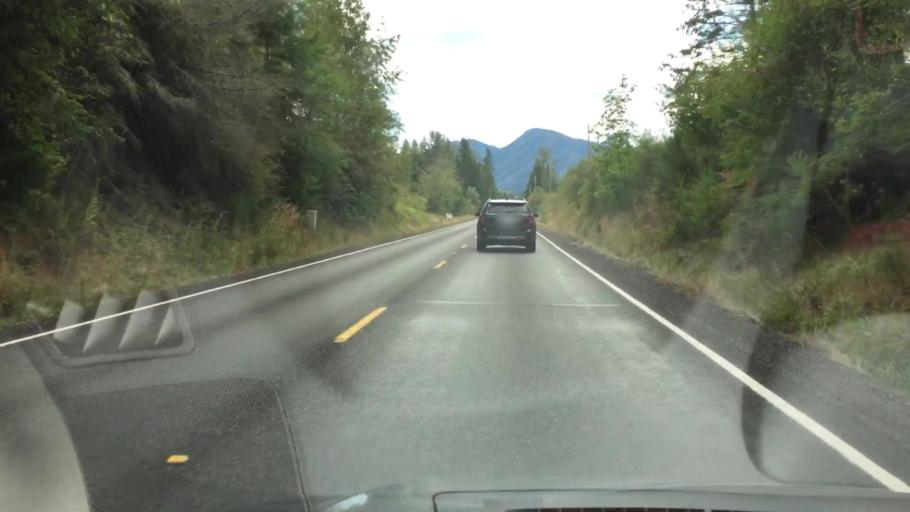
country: US
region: Washington
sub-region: Pierce County
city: Eatonville
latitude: 46.8143
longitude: -122.2665
